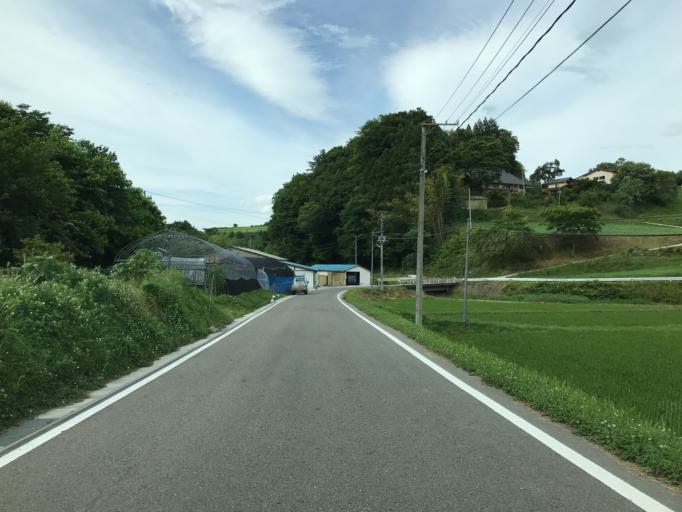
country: JP
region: Fukushima
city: Funehikimachi-funehiki
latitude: 37.4952
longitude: 140.5478
